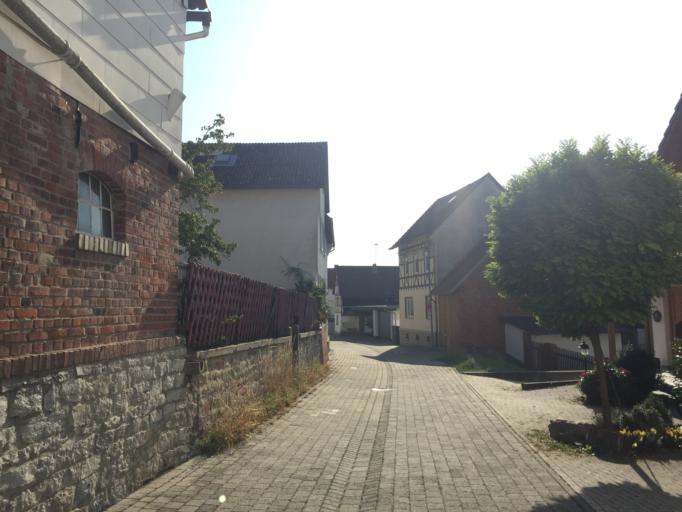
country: DE
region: Hesse
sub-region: Regierungsbezirk Giessen
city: Hoernsheim
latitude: 50.4610
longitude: 8.5870
